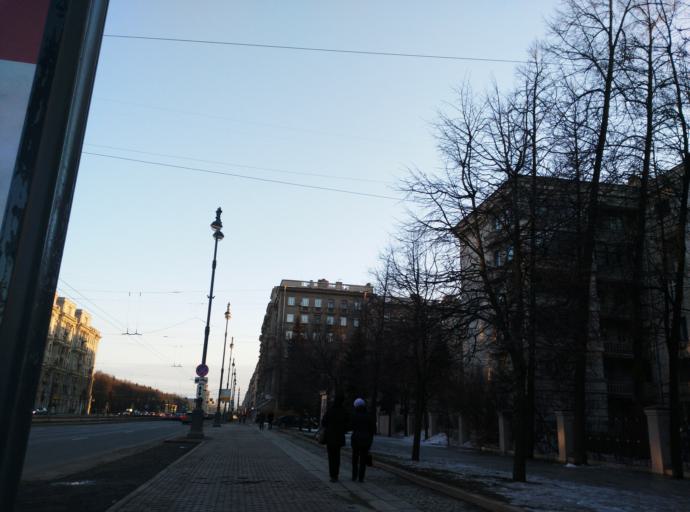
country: RU
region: St.-Petersburg
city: Kupchino
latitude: 59.8738
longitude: 30.3197
